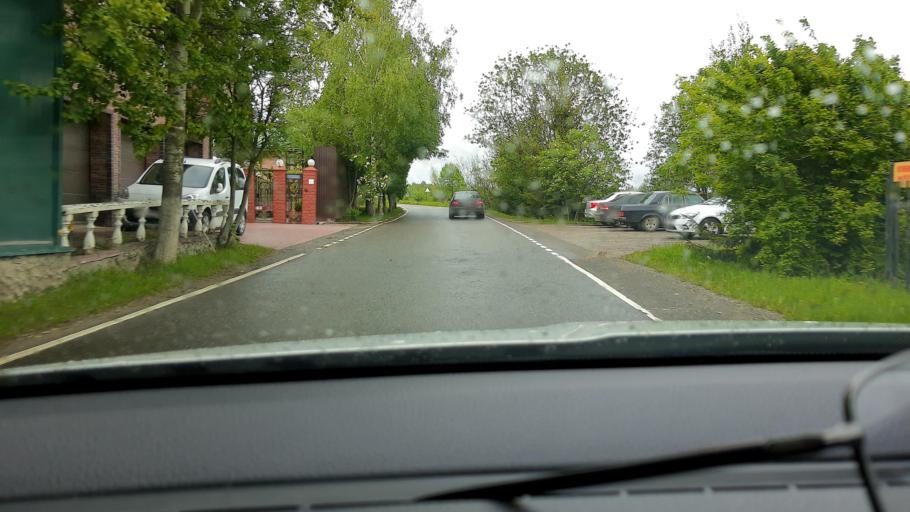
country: RU
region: Moskovskaya
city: Nikolina Gora
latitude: 55.7536
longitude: 36.9796
